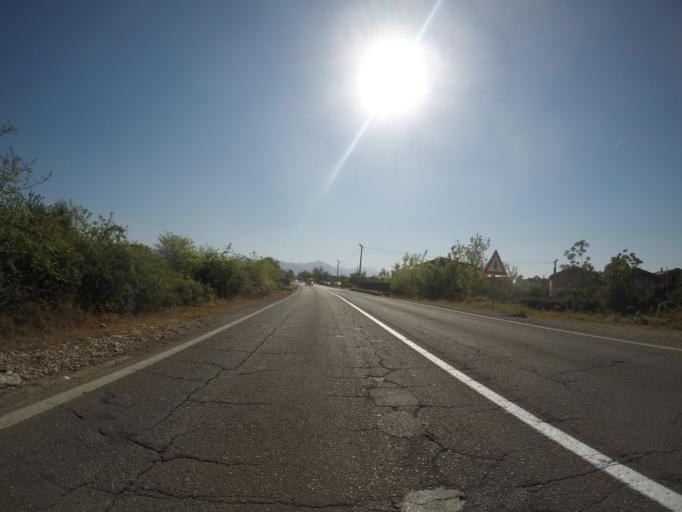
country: ME
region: Podgorica
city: Podgorica
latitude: 42.4433
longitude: 19.2065
